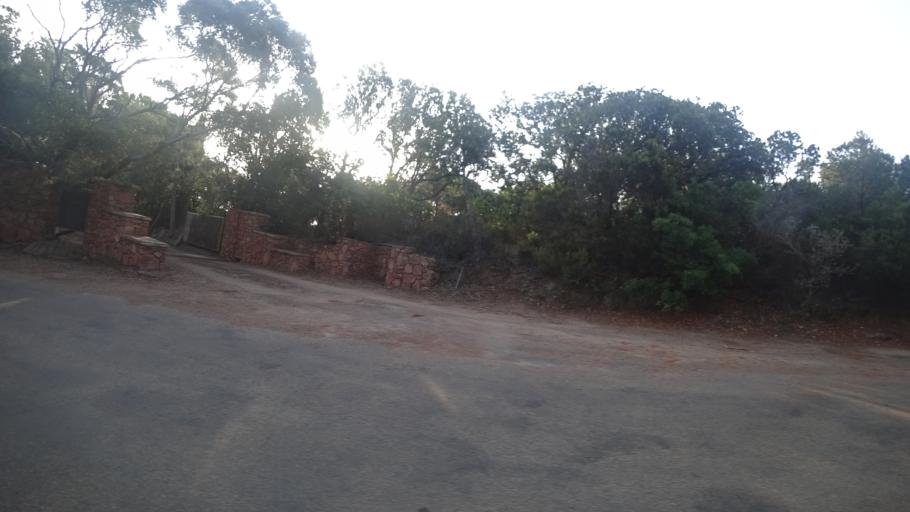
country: FR
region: Corsica
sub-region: Departement de la Corse-du-Sud
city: Porto-Vecchio
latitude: 41.6191
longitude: 9.3541
